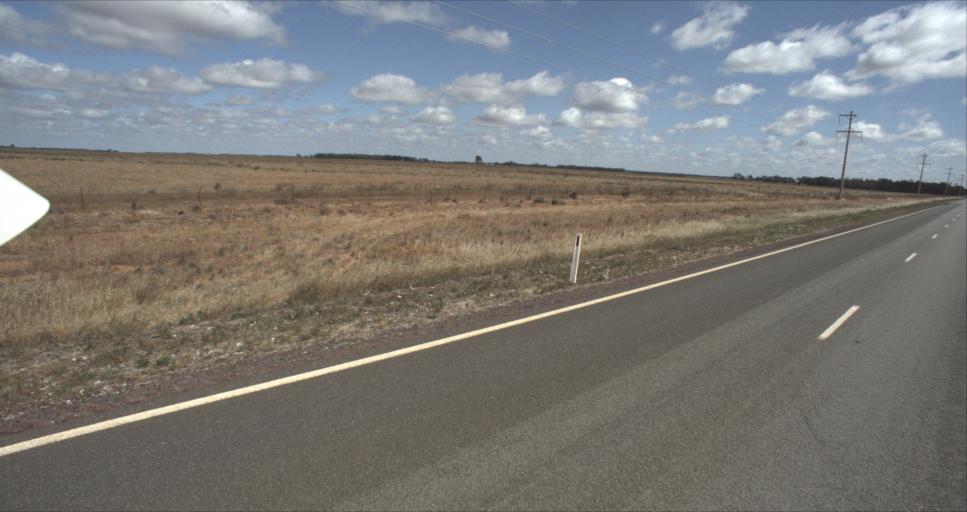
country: AU
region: New South Wales
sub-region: Murrumbidgee Shire
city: Darlington Point
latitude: -34.5843
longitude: 146.1645
